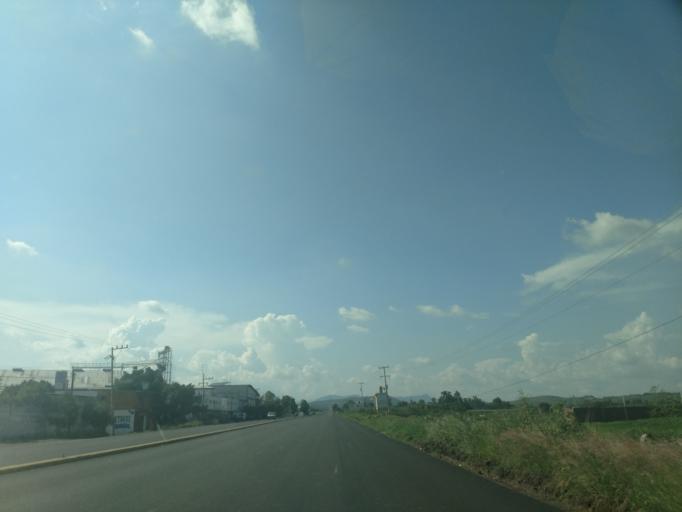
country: MX
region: Jalisco
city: Ahualulco de Mercado
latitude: 20.7087
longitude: -103.9728
